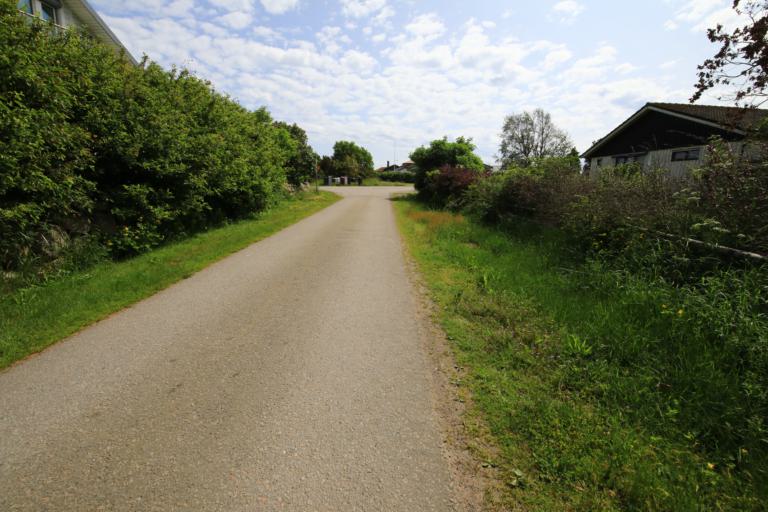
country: SE
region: Halland
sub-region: Varbergs Kommun
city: Traslovslage
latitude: 57.0719
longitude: 12.2633
